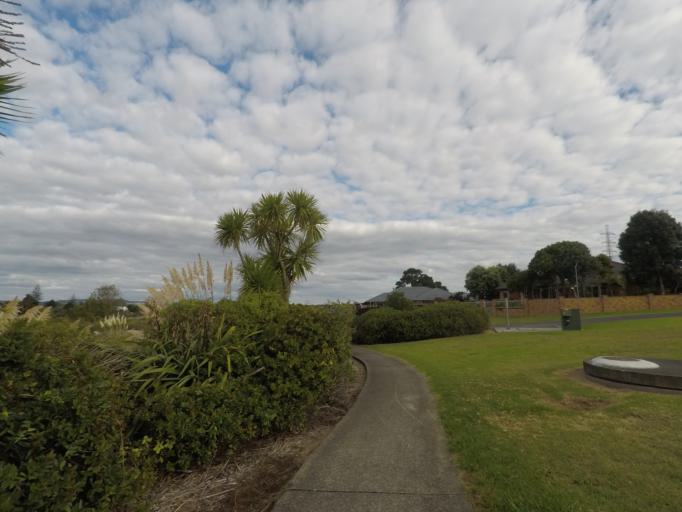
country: NZ
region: Auckland
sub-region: Auckland
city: Papakura
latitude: -37.0540
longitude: 174.9239
